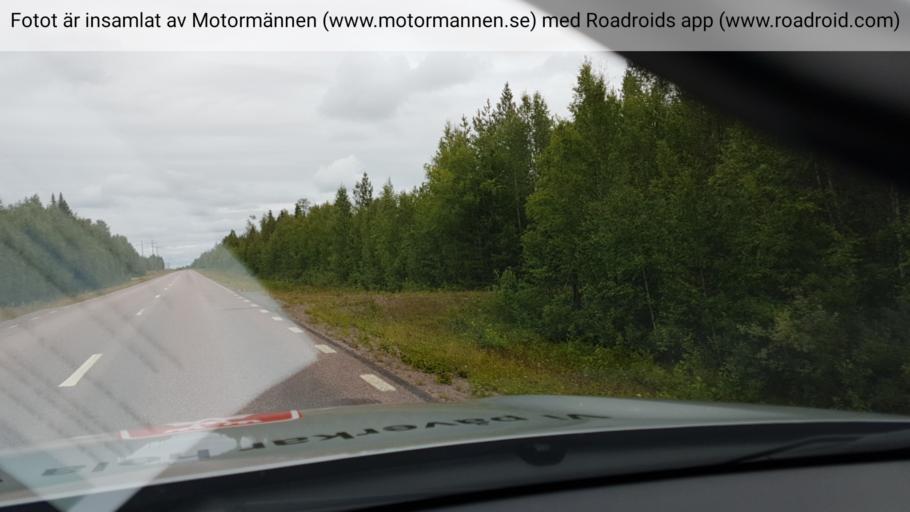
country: SE
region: Norrbotten
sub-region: Pajala Kommun
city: Pajala
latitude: 67.0910
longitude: 22.5648
